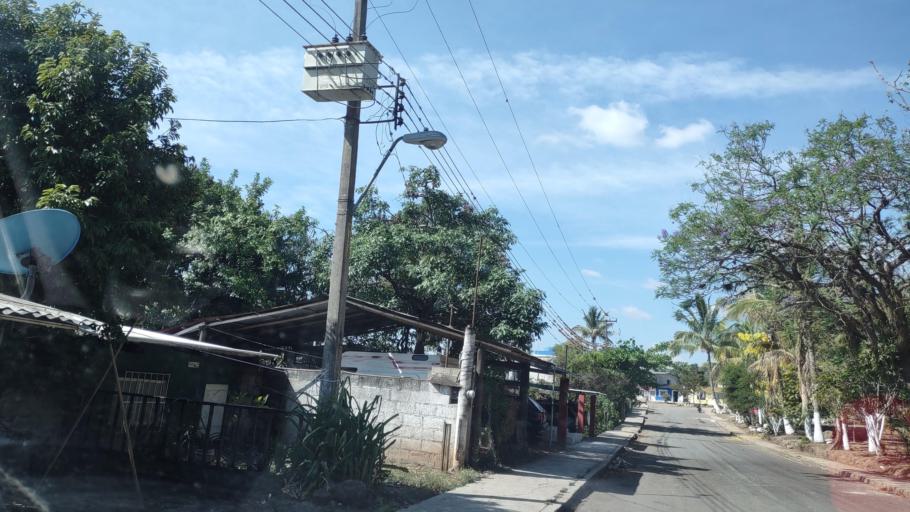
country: MX
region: Veracruz
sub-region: Coatepec
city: Tuzamapan
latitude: 19.3820
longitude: -96.9033
